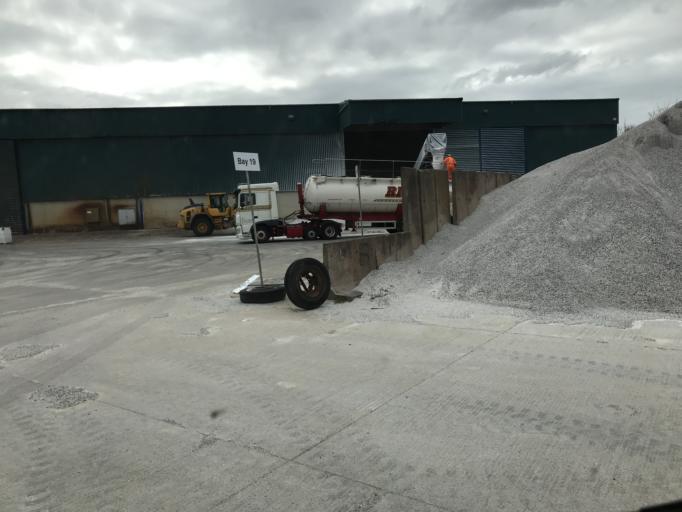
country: GB
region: England
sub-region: Metropolitan Borough of Wirral
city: Bromborough
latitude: 53.3536
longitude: -2.9098
